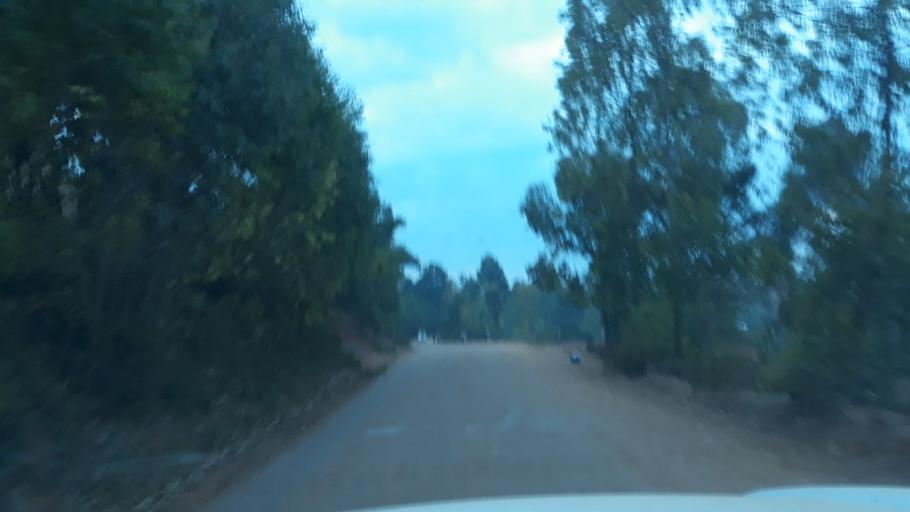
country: CD
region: South Kivu
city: Bukavu
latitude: -2.5685
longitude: 28.8567
